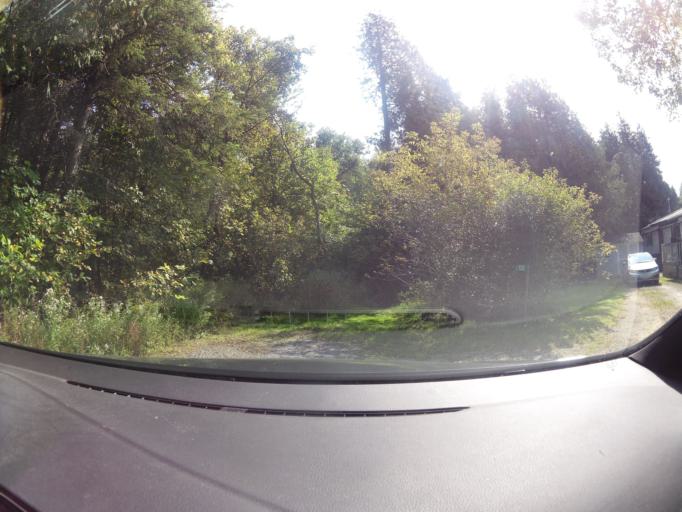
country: CA
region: Ontario
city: Arnprior
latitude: 45.3410
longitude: -76.2073
